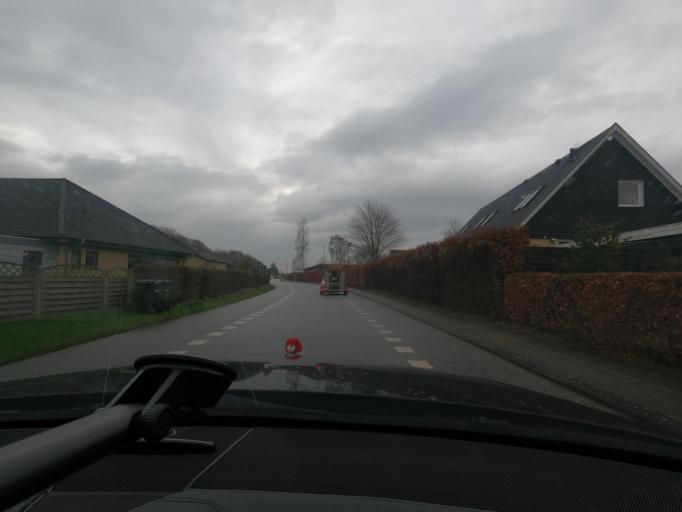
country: DK
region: South Denmark
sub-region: Sonderborg Kommune
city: Horuphav
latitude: 54.9133
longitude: 9.8938
